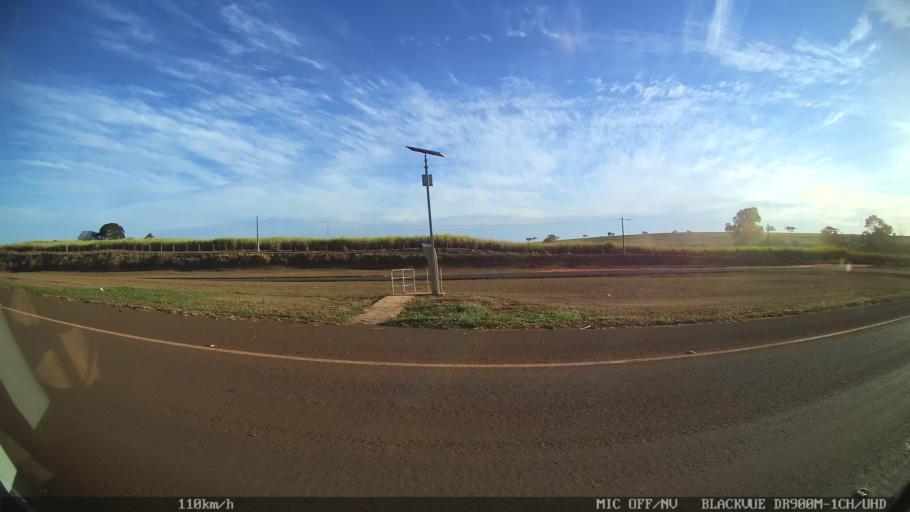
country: BR
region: Sao Paulo
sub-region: Guapiacu
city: Guapiacu
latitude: -21.0112
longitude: -49.1797
